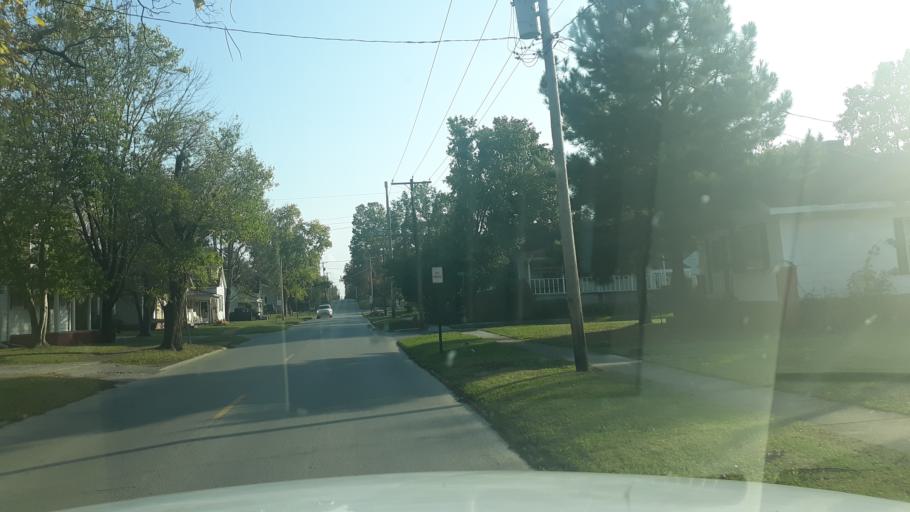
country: US
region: Illinois
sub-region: Saline County
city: Harrisburg
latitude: 37.7297
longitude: -88.5403
